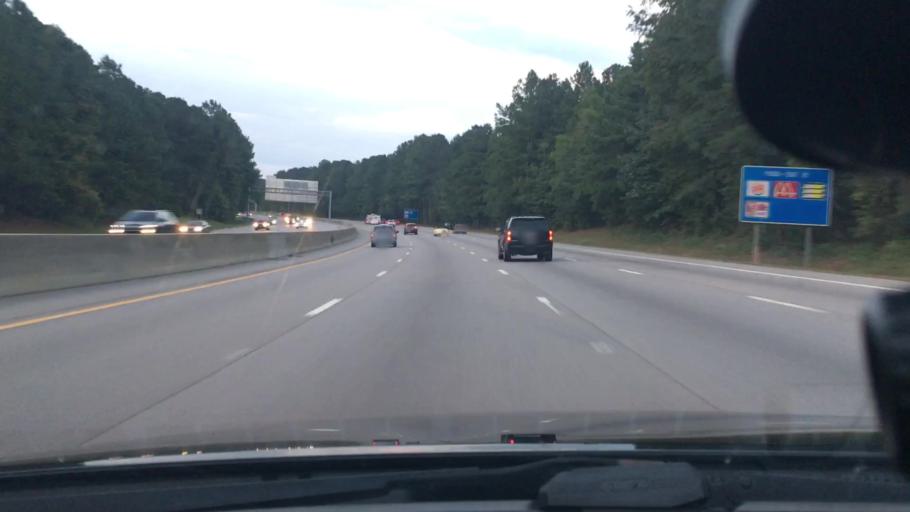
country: US
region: North Carolina
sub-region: Wake County
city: Garner
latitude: 35.7586
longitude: -78.5761
